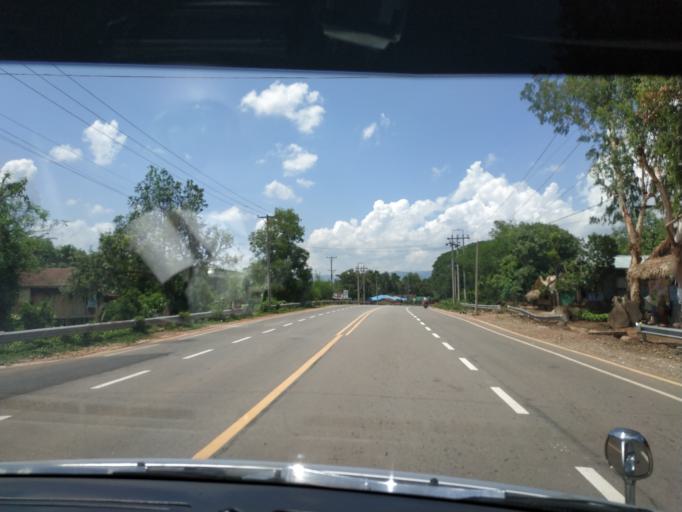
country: MM
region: Mon
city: Kyaikto
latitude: 17.3449
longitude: 97.0371
